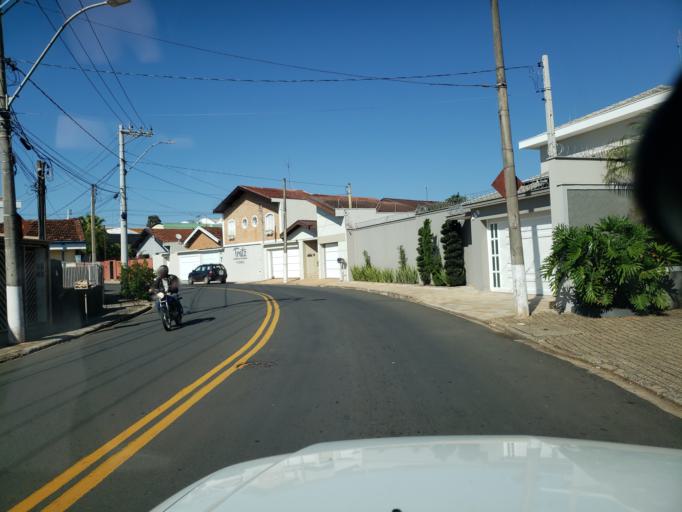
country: BR
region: Sao Paulo
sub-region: Itapira
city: Itapira
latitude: -22.4426
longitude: -46.8321
